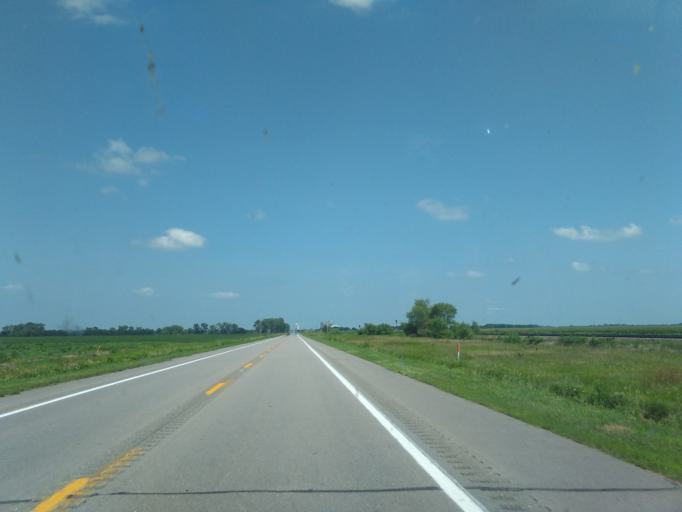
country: US
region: Nebraska
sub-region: Phelps County
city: Holdrege
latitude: 40.7239
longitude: -99.4243
